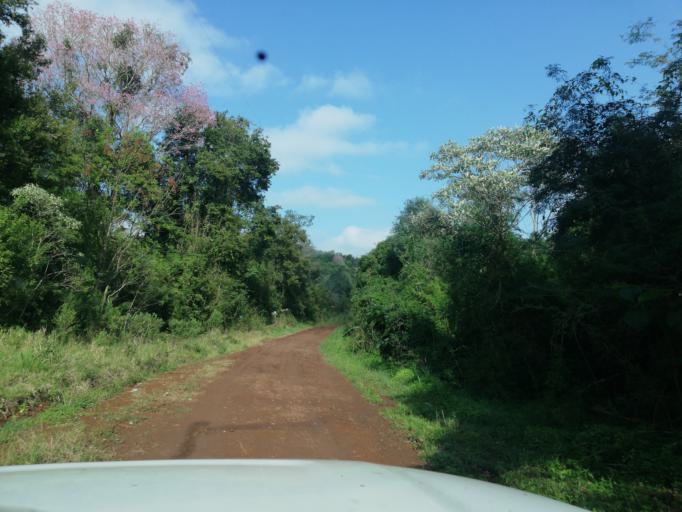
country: AR
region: Misiones
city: Cerro Azul
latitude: -27.6015
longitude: -55.5316
